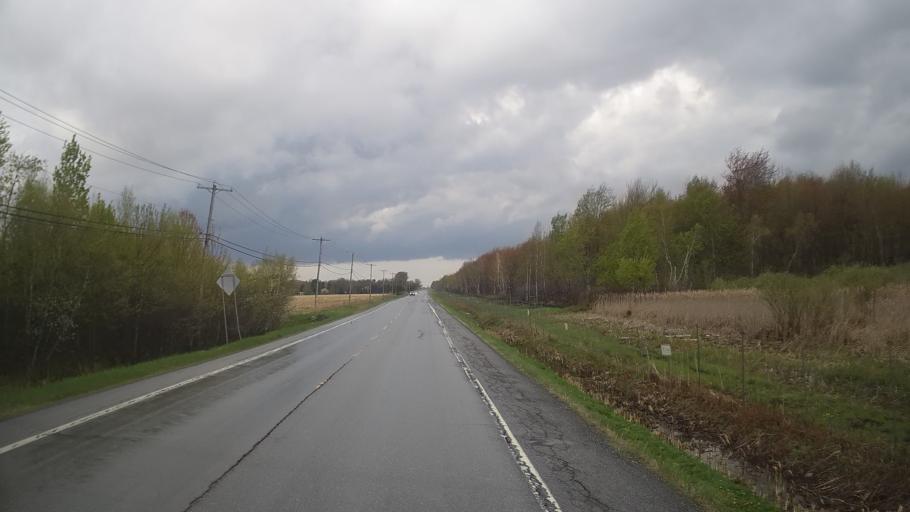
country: CA
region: Quebec
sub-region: Monteregie
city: Farnham
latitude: 45.2950
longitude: -73.0243
